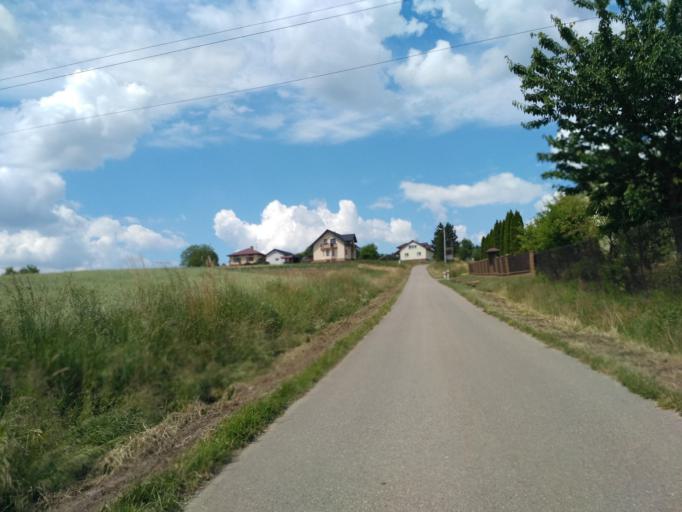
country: PL
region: Subcarpathian Voivodeship
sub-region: Powiat jasielski
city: Brzyska
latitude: 49.8018
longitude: 21.3949
